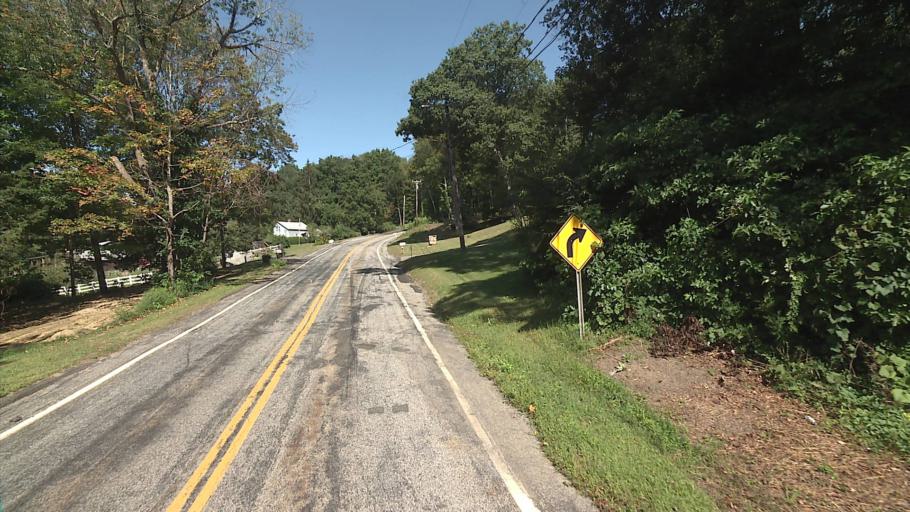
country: US
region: Connecticut
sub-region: Litchfield County
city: Thomaston
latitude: 41.7138
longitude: -73.0687
